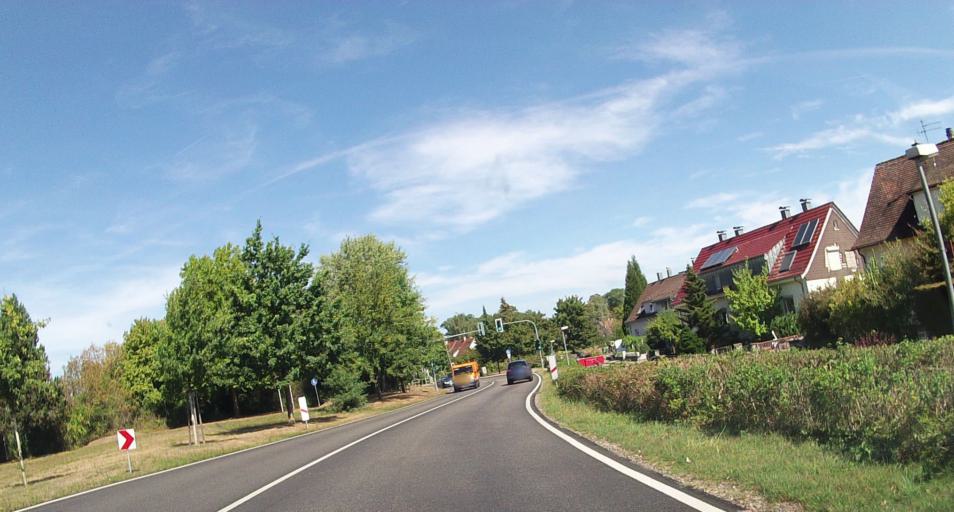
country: DE
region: Baden-Wuerttemberg
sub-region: Karlsruhe Region
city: Rastatt
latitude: 48.8422
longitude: 8.2037
